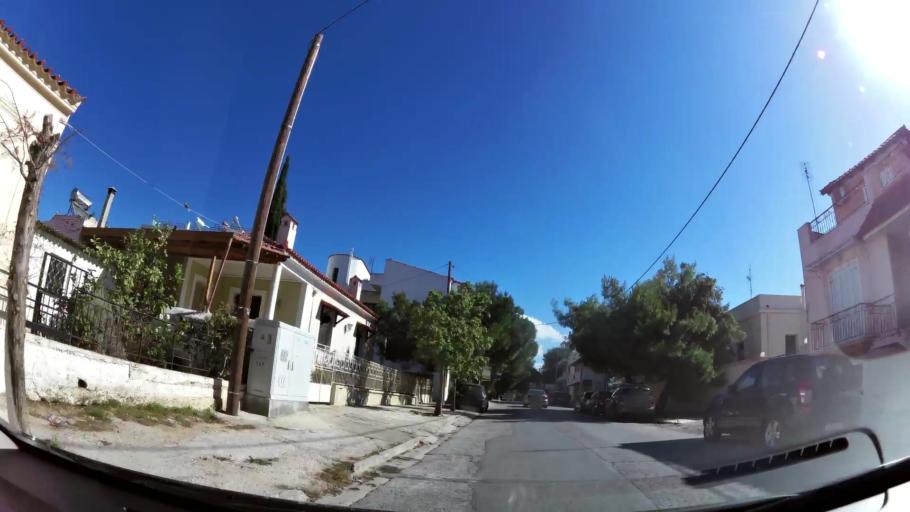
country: GR
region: Attica
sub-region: Nomarchia Anatolikis Attikis
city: Markopoulo
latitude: 37.8861
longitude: 23.9356
